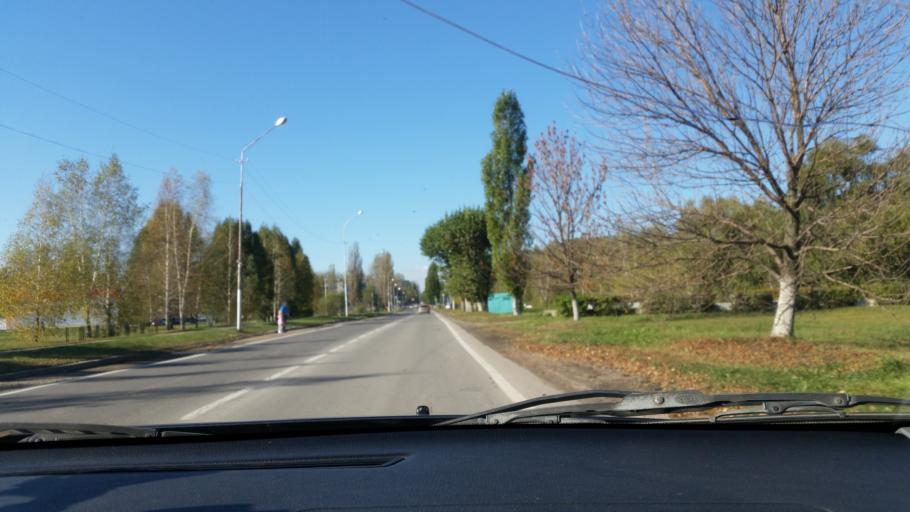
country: RU
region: Lipetsk
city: Gryazi
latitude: 52.4892
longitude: 39.9706
